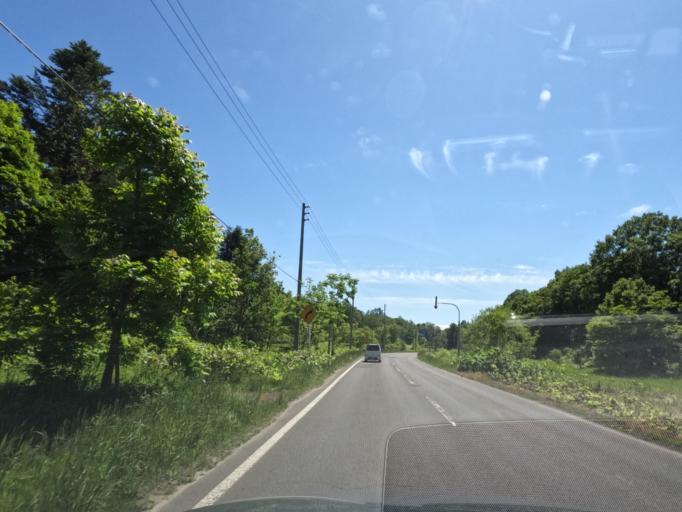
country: JP
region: Hokkaido
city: Iwamizawa
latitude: 43.0970
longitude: 141.7657
